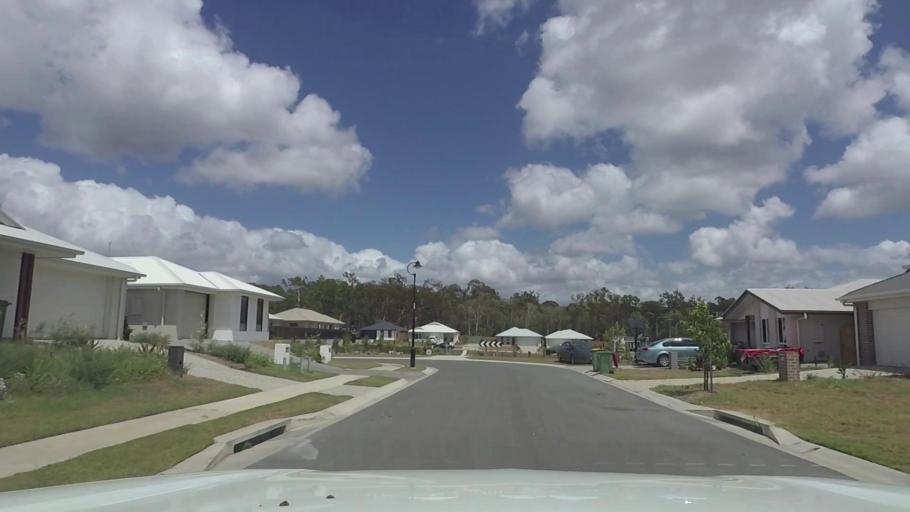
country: AU
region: Queensland
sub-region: Logan
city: Logan Reserve
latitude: -27.7075
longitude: 153.0805
